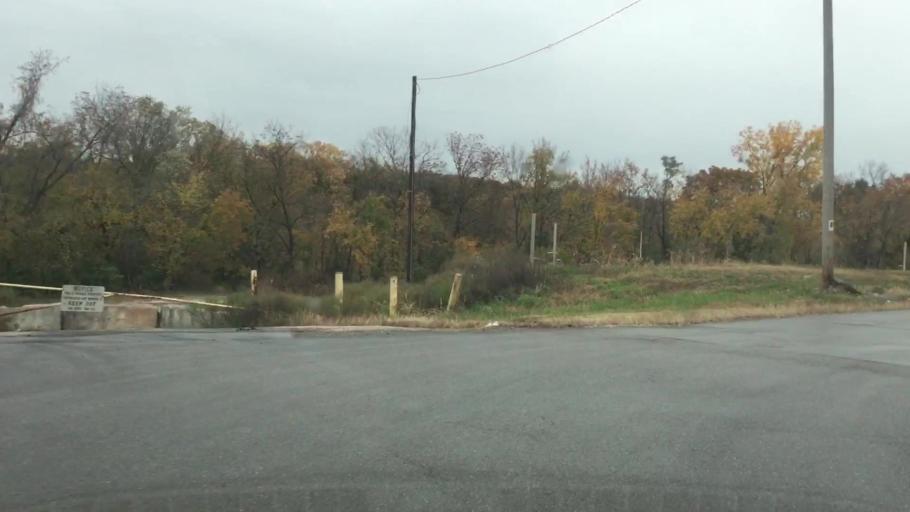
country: US
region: Kansas
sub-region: Wyandotte County
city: Edwardsville
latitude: 38.9999
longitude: -94.8233
